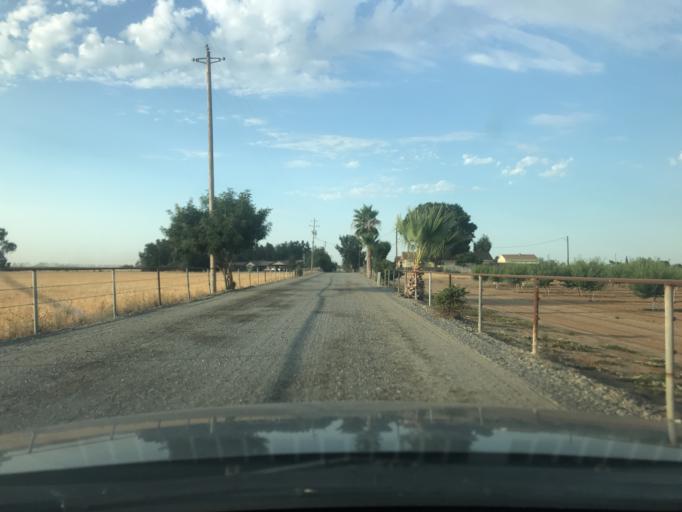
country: US
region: California
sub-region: Merced County
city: Merced
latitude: 37.3711
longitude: -120.4986
